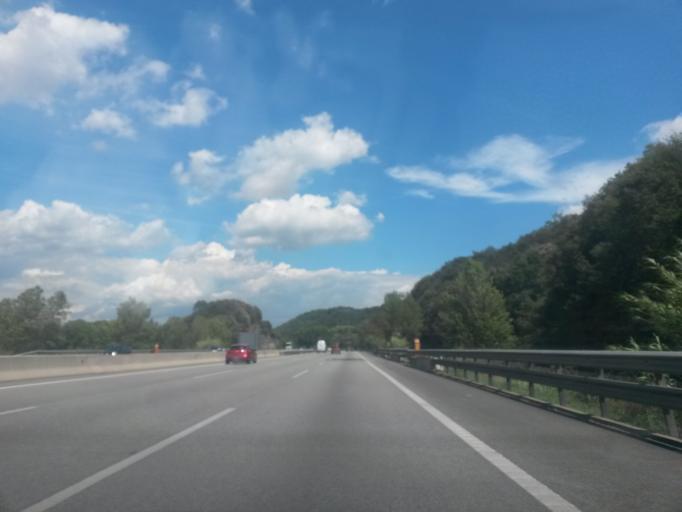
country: ES
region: Catalonia
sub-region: Provincia de Barcelona
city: Sant Celoni
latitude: 41.6831
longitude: 2.4947
